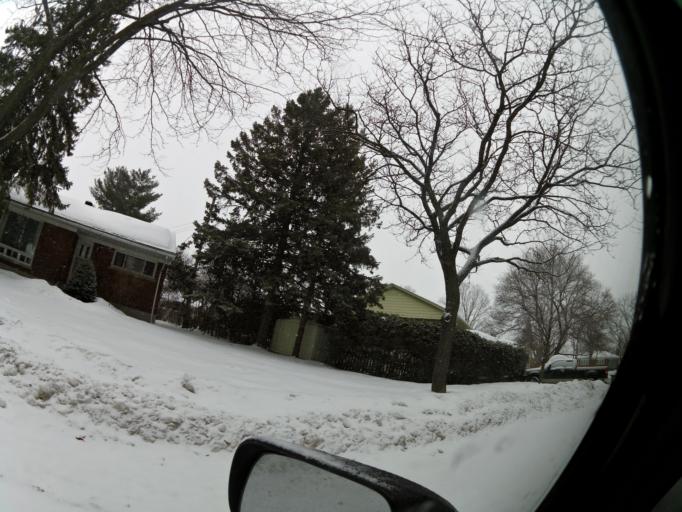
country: CA
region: Ontario
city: Ottawa
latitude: 45.4063
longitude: -75.6417
